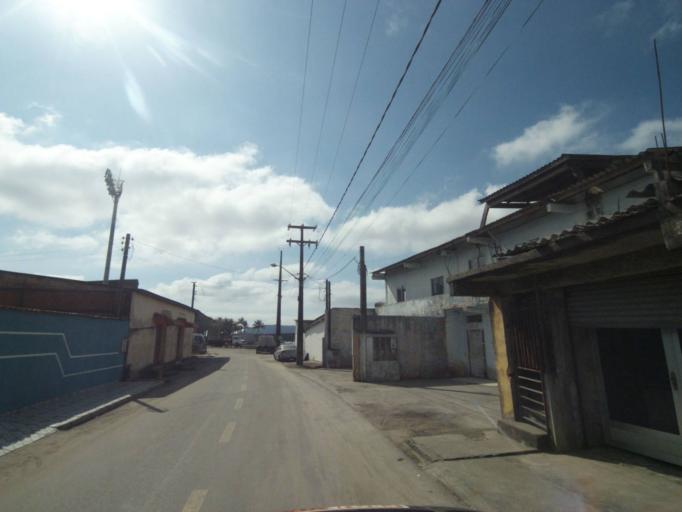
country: BR
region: Parana
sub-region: Paranagua
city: Paranagua
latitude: -25.5257
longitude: -48.5078
